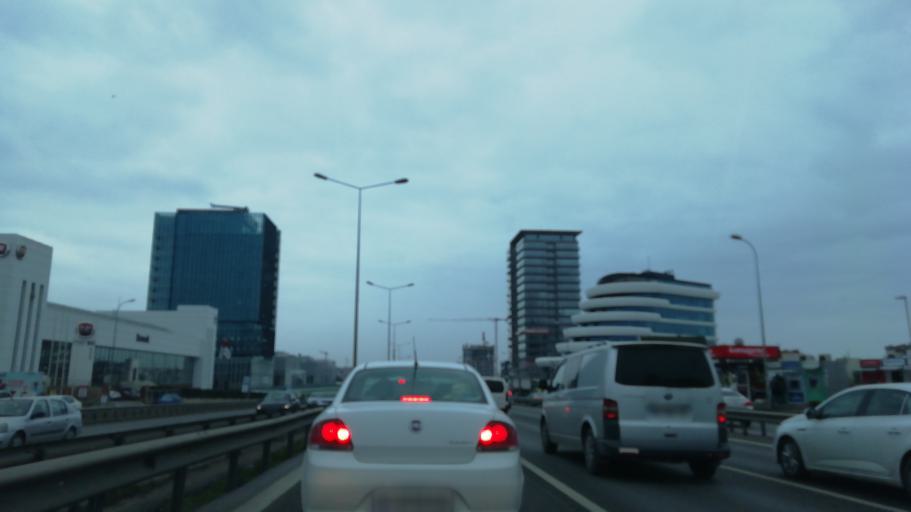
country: TR
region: Istanbul
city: Pendik
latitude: 40.8970
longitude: 29.2252
